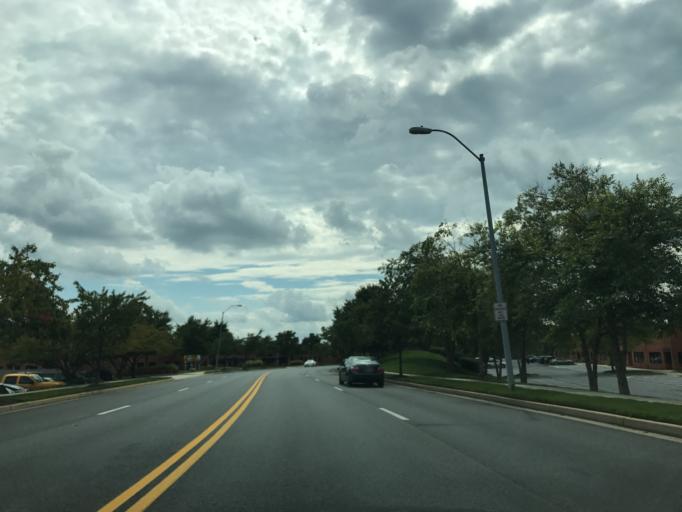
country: US
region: Maryland
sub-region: Baltimore County
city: Woodlawn
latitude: 39.3252
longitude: -76.7504
